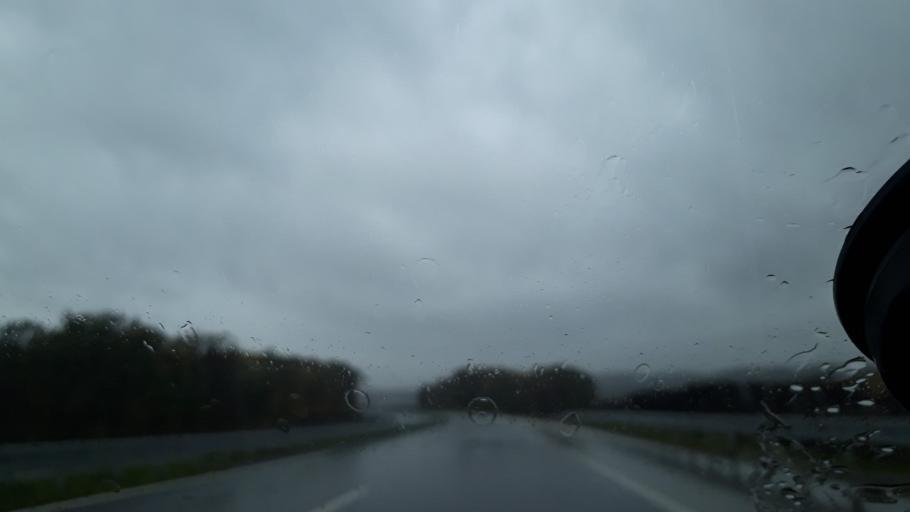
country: BA
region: Republika Srpska
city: Prnjavor
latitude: 44.8557
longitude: 17.7157
